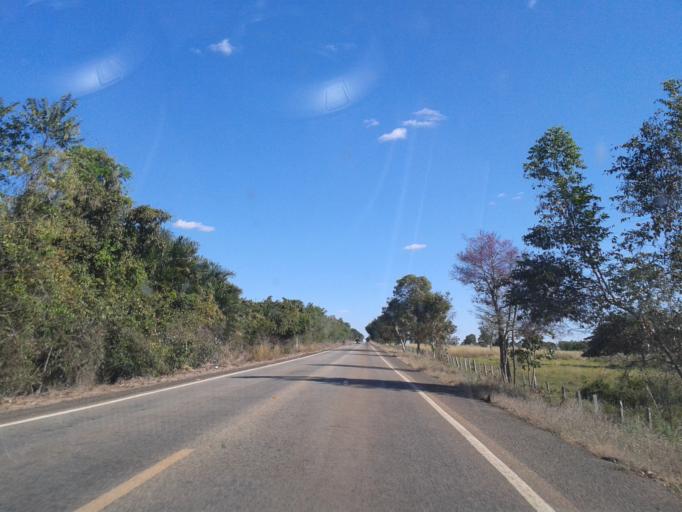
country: BR
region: Goias
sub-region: Mozarlandia
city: Mozarlandia
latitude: -14.5856
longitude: -50.5062
